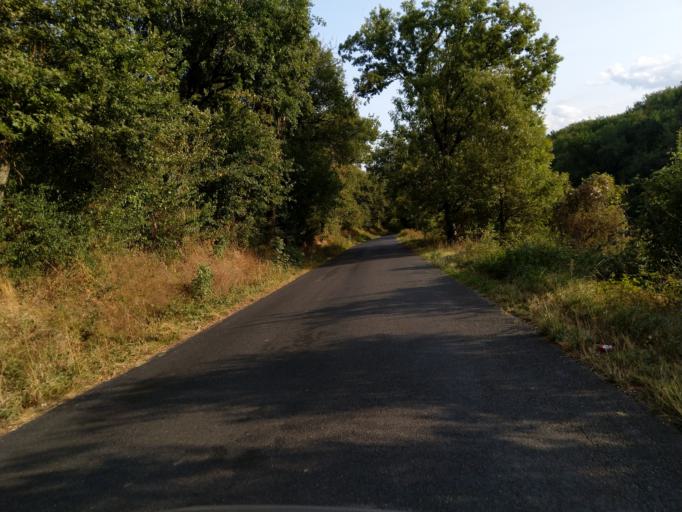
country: FR
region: Midi-Pyrenees
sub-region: Departement du Tarn
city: Frejairolles
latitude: 43.8591
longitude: 2.2341
